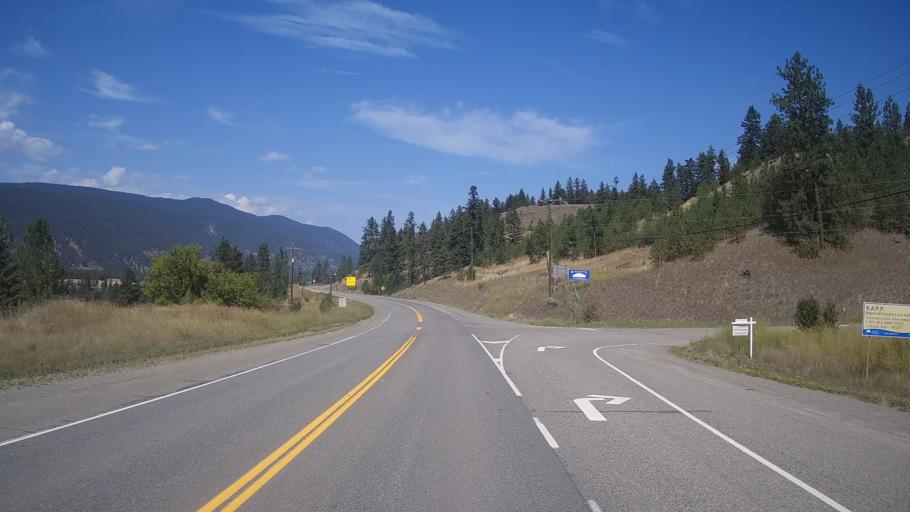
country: CA
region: British Columbia
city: Kamloops
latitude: 50.8680
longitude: -120.2625
